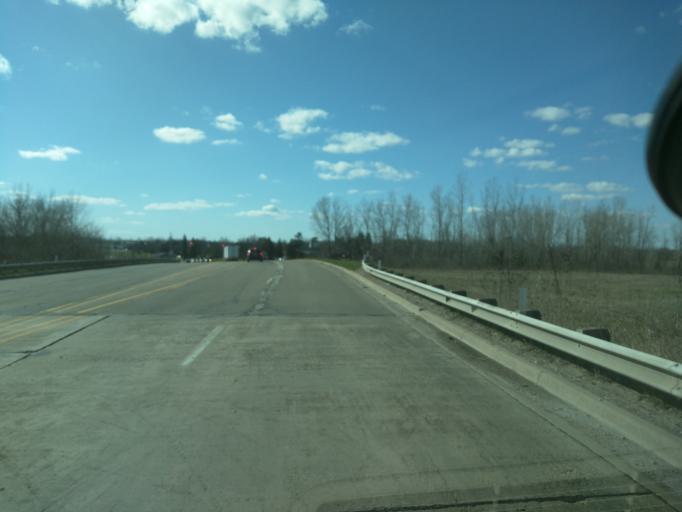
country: US
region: Michigan
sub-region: Ingham County
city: Edgemont Park
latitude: 42.7717
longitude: -84.6056
